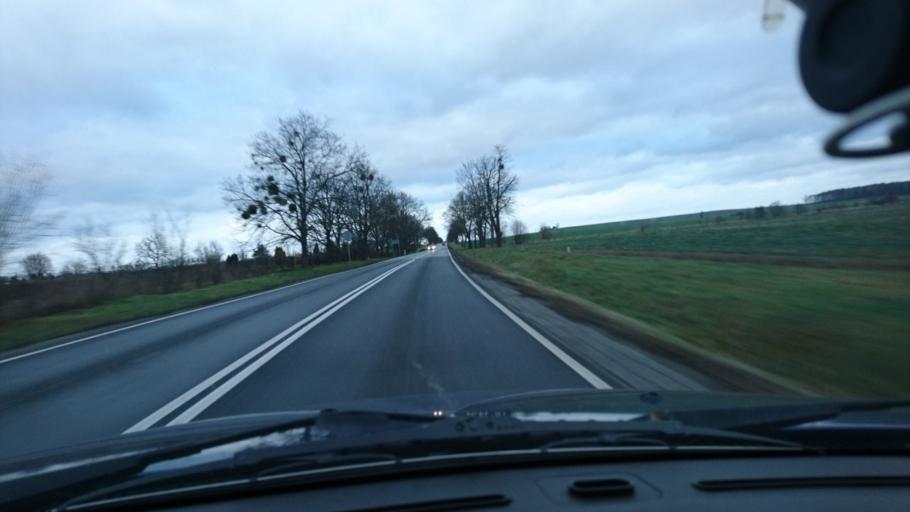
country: PL
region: Opole Voivodeship
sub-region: Powiat kluczborski
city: Byczyna
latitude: 51.0846
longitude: 18.1982
